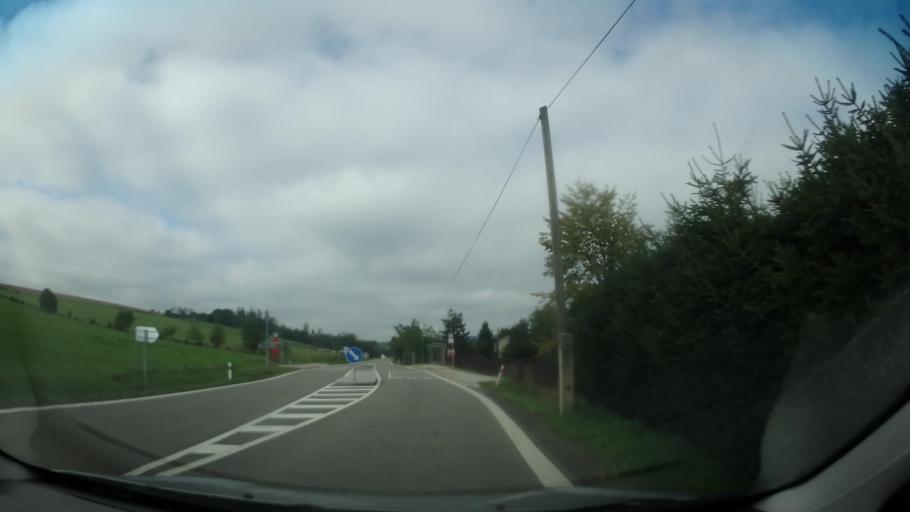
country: CZ
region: Central Bohemia
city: Bystrice
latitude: 49.7549
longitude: 14.6103
